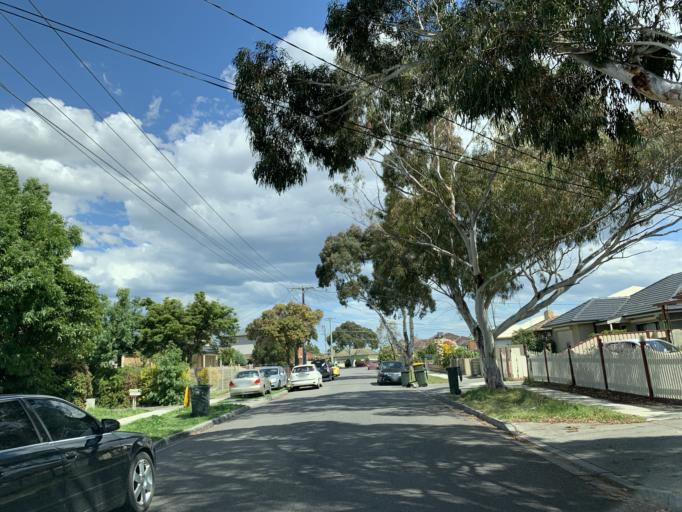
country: AU
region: Victoria
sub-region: Brimbank
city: Sunshine North
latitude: -37.7643
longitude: 144.8274
